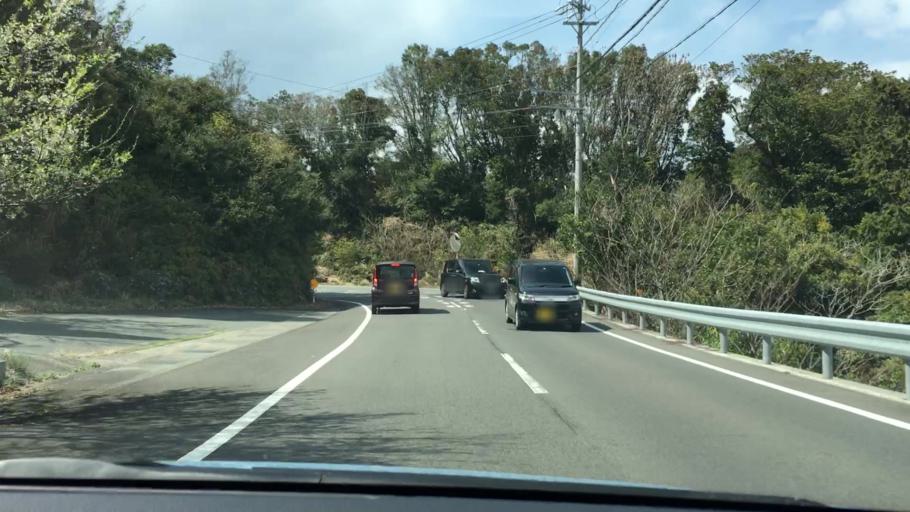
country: JP
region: Mie
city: Toba
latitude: 34.4539
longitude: 136.8743
